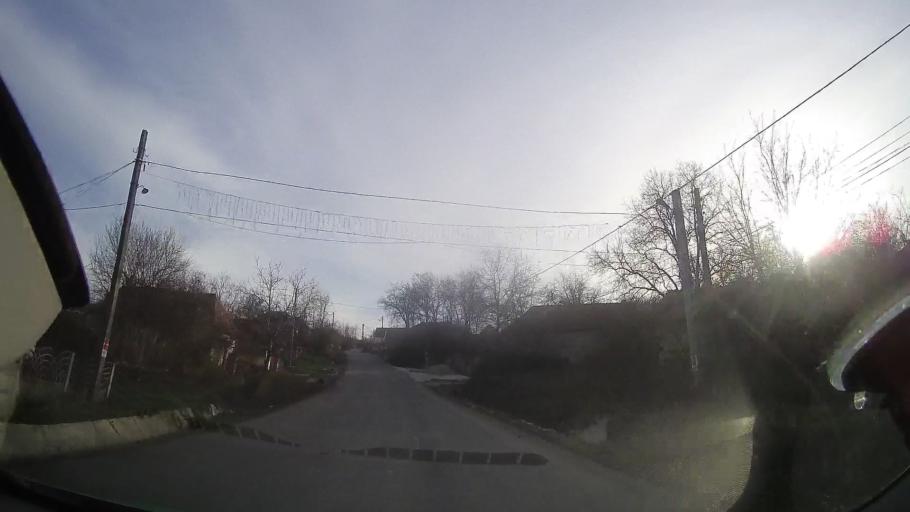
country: RO
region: Bihor
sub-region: Comuna Sarbi
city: Burzuc
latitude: 47.1066
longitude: 22.1710
